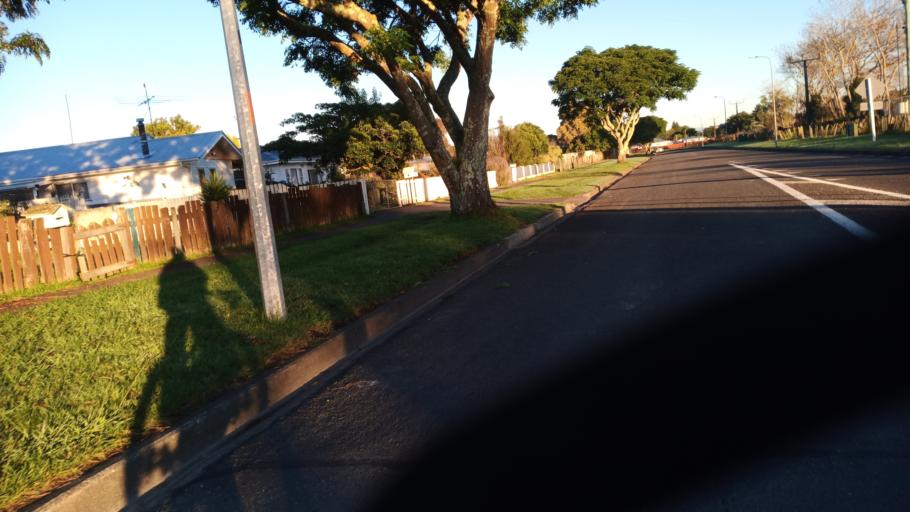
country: NZ
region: Gisborne
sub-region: Gisborne District
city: Gisborne
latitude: -38.6601
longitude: 177.9942
